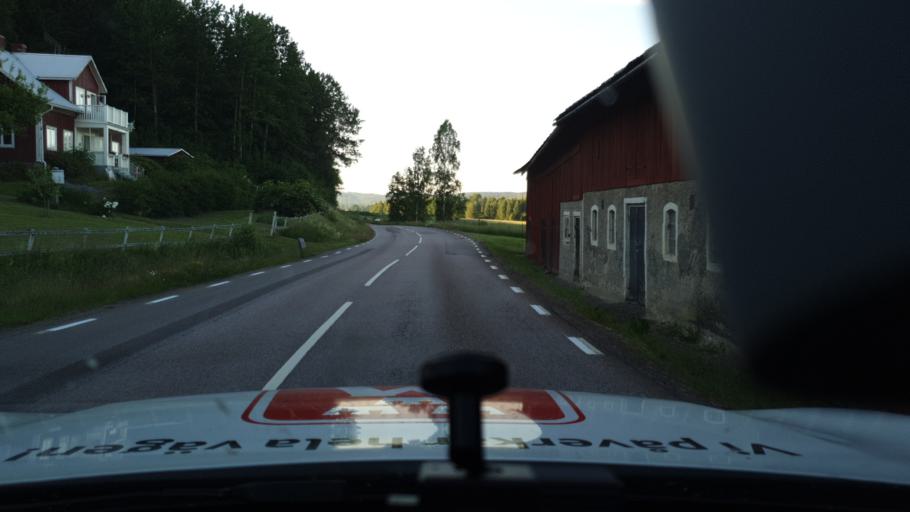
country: SE
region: Vaermland
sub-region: Kils Kommun
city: Kil
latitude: 59.5949
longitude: 13.3142
